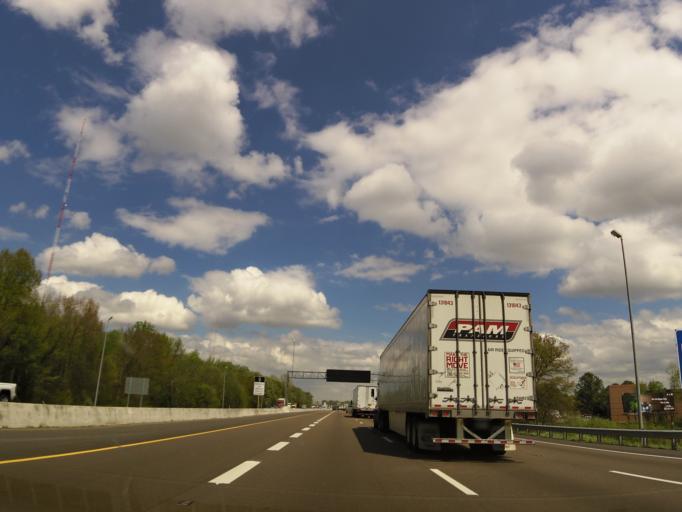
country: US
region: Tennessee
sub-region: Shelby County
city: Bartlett
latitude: 35.1700
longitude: -89.8486
